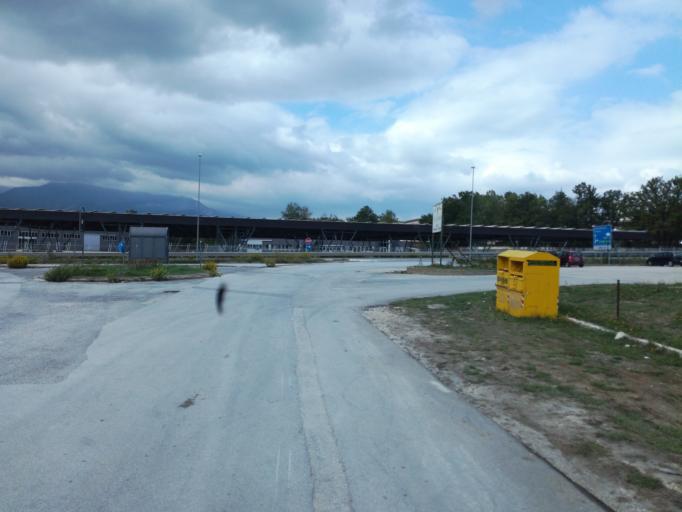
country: IT
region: Molise
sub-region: Provincia di Campobasso
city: Guardiaregia
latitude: 41.4699
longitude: 14.5599
